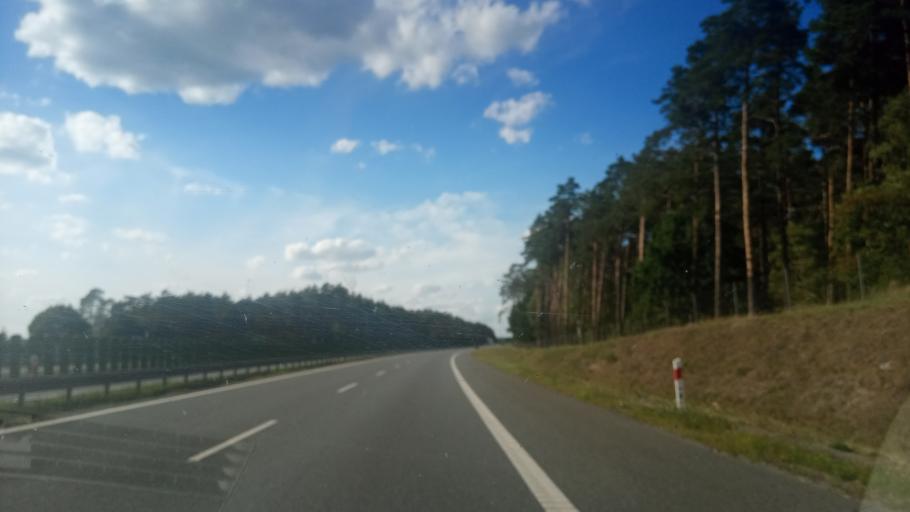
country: PL
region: Kujawsko-Pomorskie
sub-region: Powiat bydgoski
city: Biale Blota
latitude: 53.0761
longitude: 17.9148
